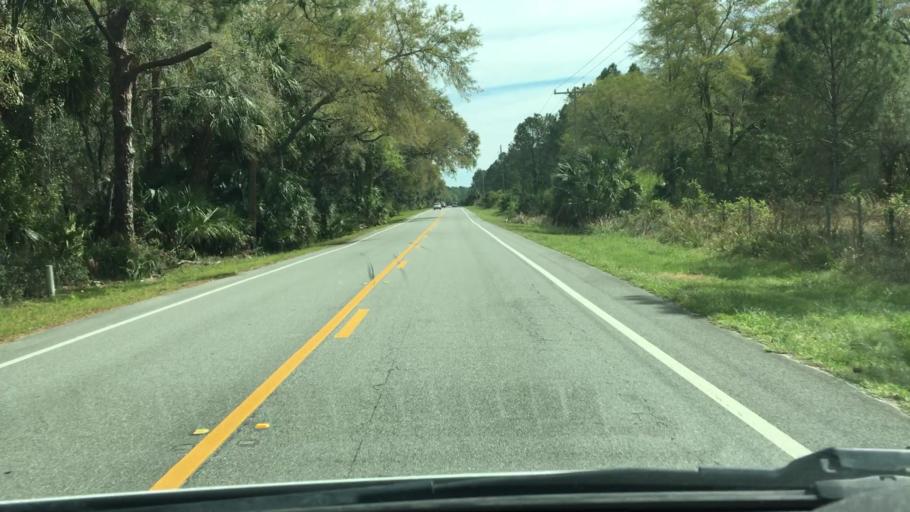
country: US
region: Florida
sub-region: Lake County
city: Lake Mack-Forest Hills
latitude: 29.0090
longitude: -81.4062
